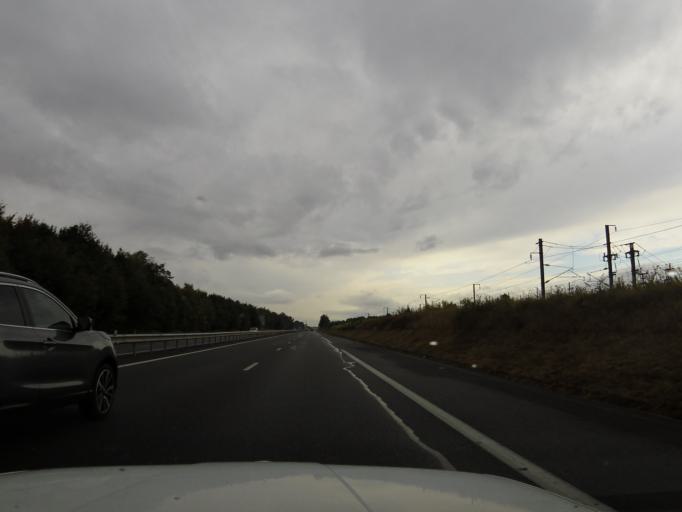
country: FR
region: Rhone-Alpes
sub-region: Departement du Rhone
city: Jons
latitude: 45.7849
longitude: 5.0808
